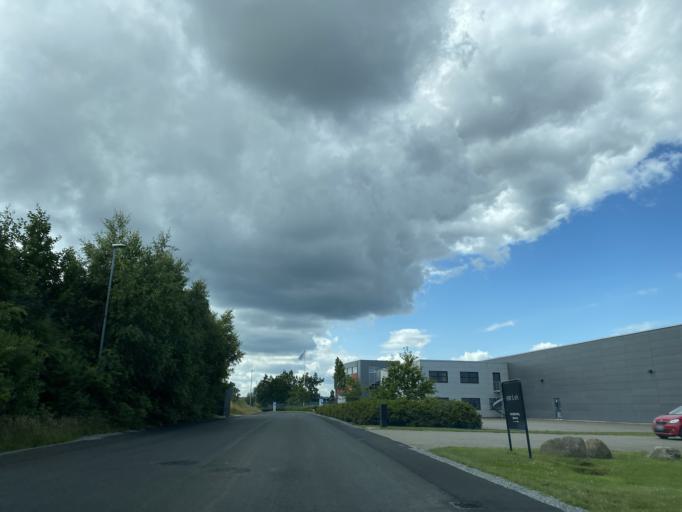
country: DK
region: Central Jutland
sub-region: Silkeborg Kommune
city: Silkeborg
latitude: 56.2060
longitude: 9.5786
